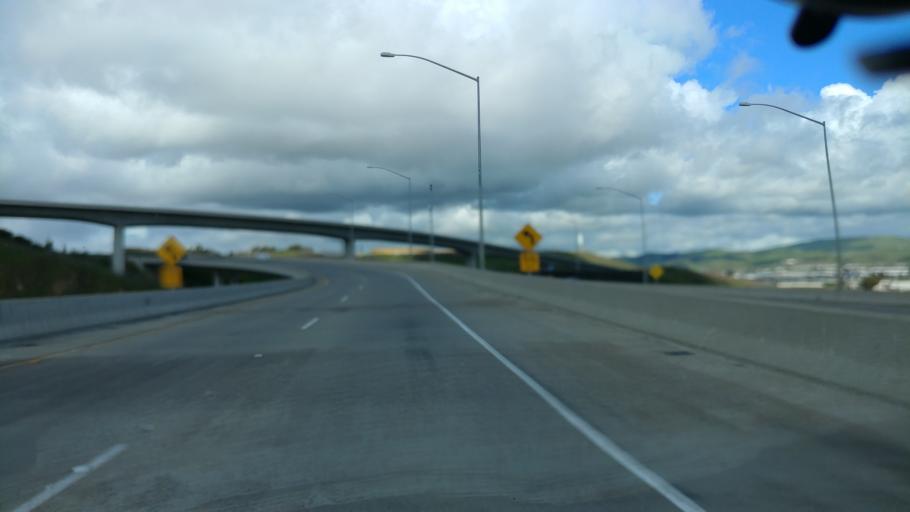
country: US
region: California
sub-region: Solano County
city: Benicia
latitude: 38.0499
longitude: -122.1273
